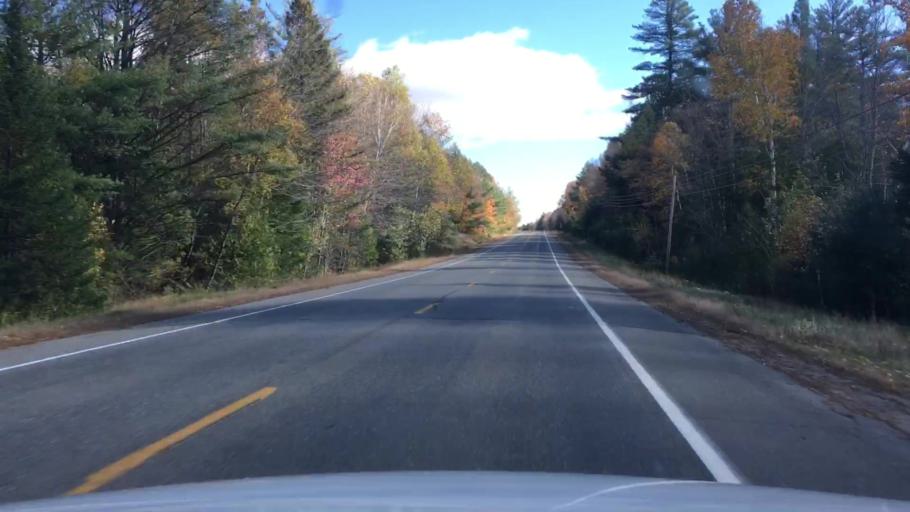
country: US
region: Maine
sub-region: Penobscot County
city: Millinocket
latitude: 45.6568
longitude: -68.6638
